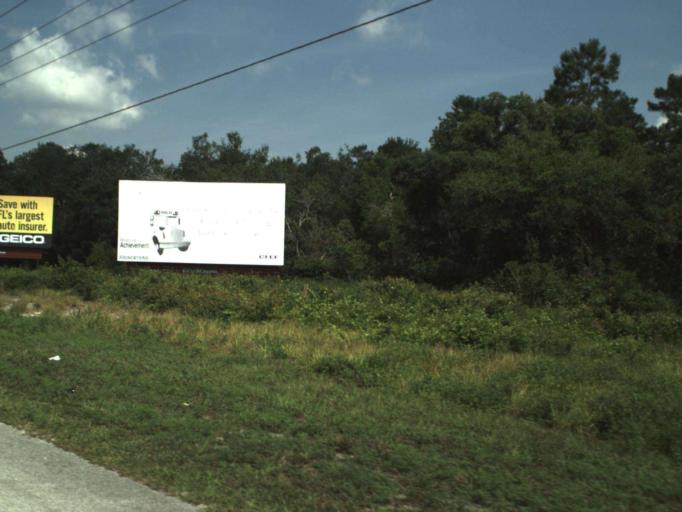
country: US
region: Florida
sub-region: Volusia County
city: Lake Helen
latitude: 29.0176
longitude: -81.2384
